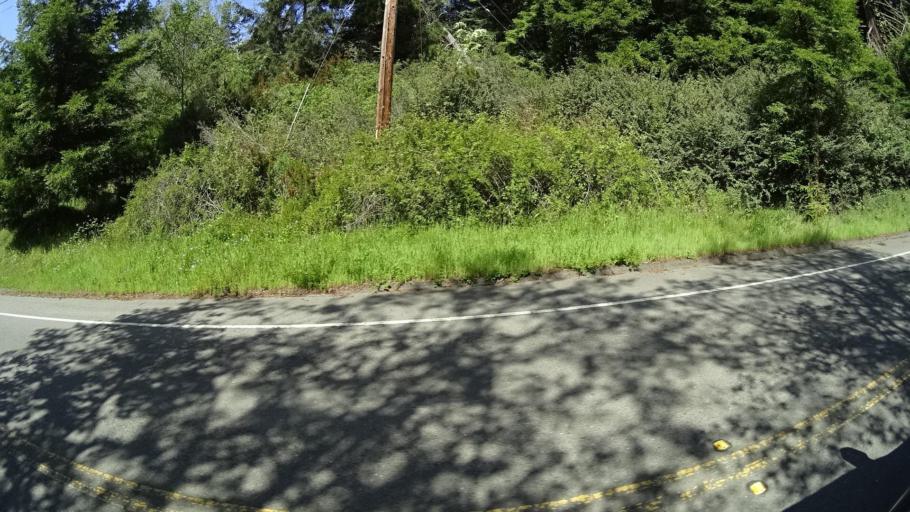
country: US
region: California
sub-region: Humboldt County
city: Hydesville
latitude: 40.5702
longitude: -124.1221
